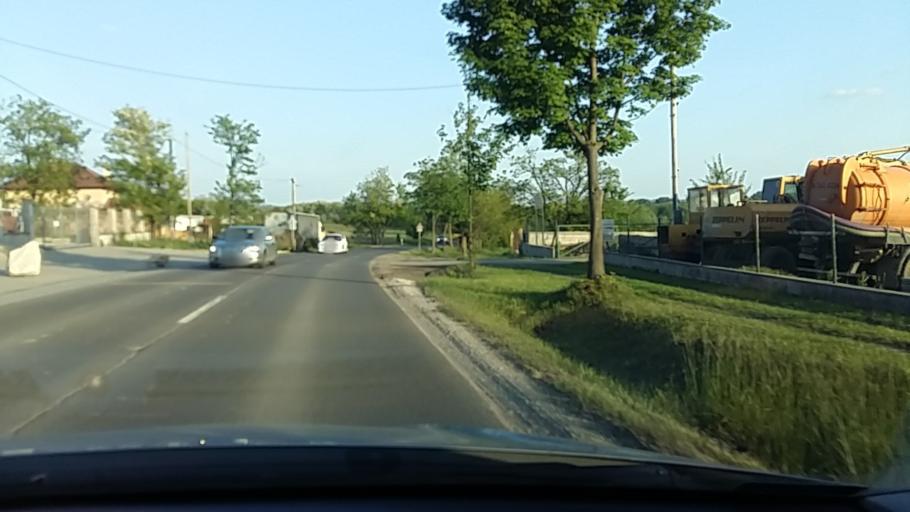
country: HU
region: Pest
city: Orbottyan
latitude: 47.6752
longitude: 19.2697
